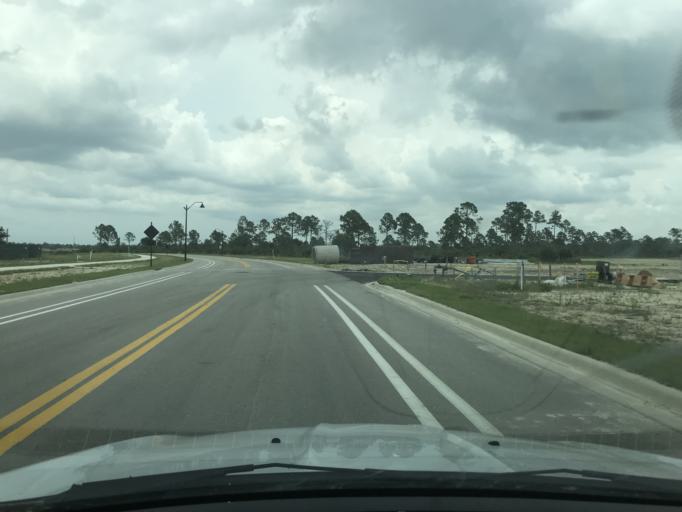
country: US
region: Florida
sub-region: Lee County
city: Olga
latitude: 26.7911
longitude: -81.7346
